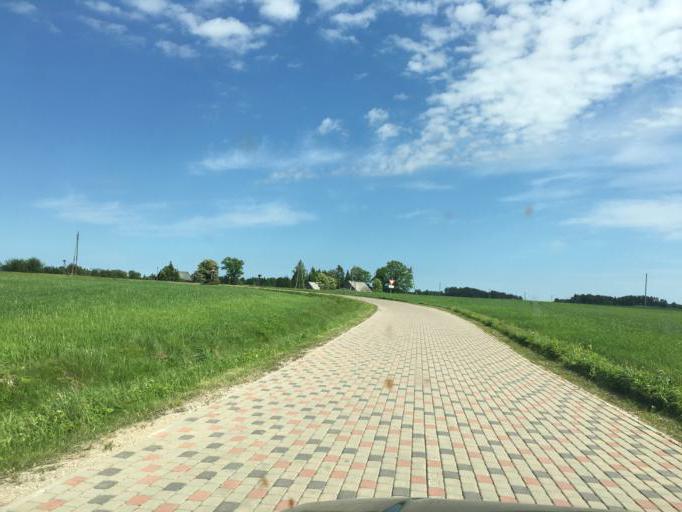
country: LV
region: Talsu Rajons
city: Valdemarpils
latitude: 57.3757
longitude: 22.5201
